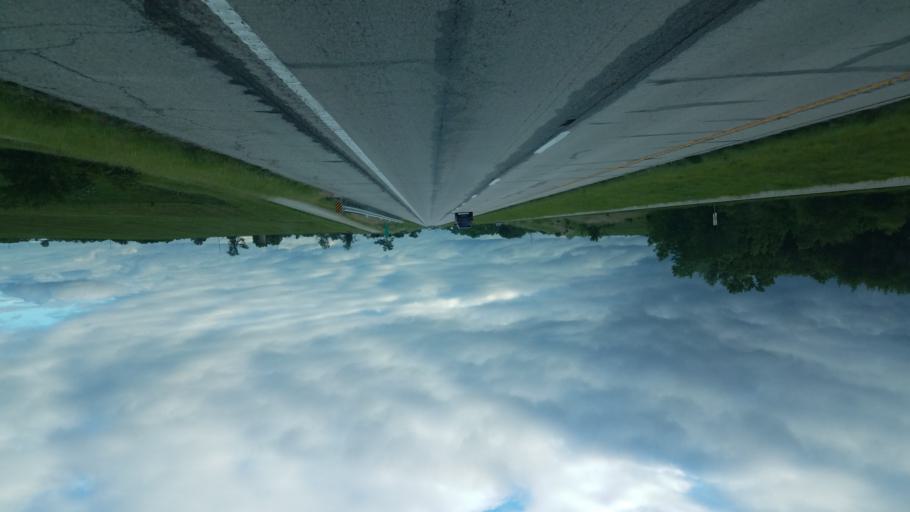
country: US
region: Missouri
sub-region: Harrison County
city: Bethany
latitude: 40.3191
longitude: -94.0115
